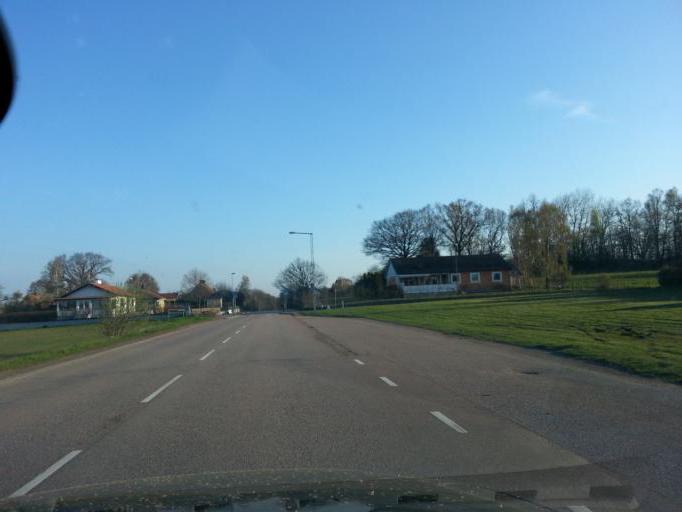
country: SE
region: Skane
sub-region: Klippans Kommun
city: Klippan
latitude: 56.1177
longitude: 13.1510
